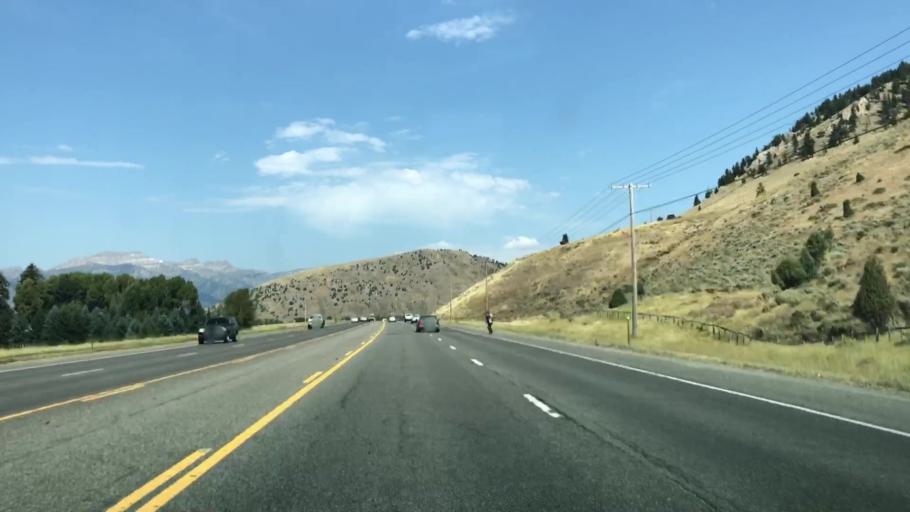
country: US
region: Wyoming
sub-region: Teton County
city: Rafter J Ranch
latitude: 43.4487
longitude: -110.7907
